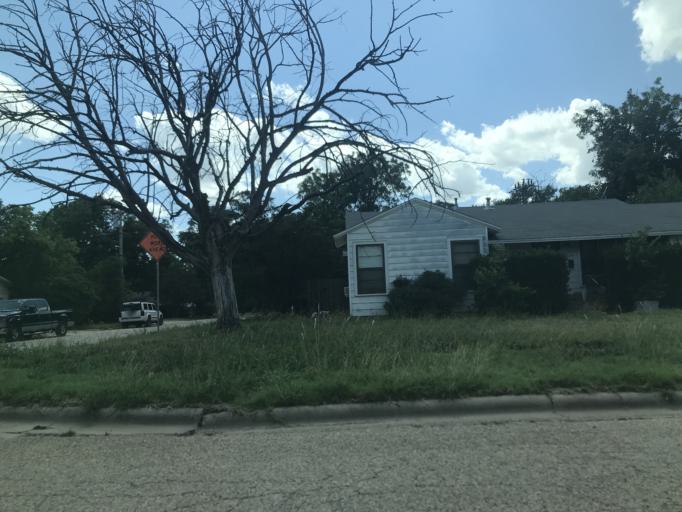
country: US
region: Texas
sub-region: Taylor County
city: Abilene
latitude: 32.4289
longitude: -99.7624
